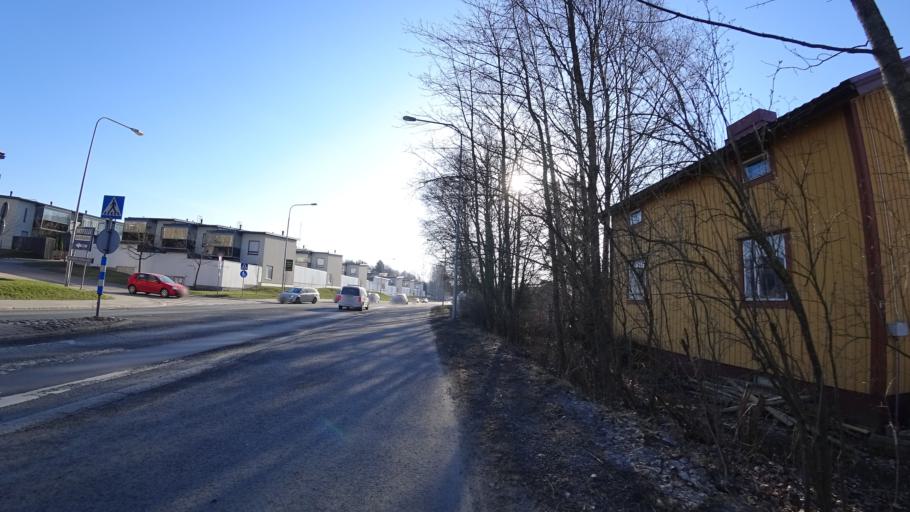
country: FI
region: Pirkanmaa
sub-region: Tampere
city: Pirkkala
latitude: 61.5088
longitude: 23.6769
